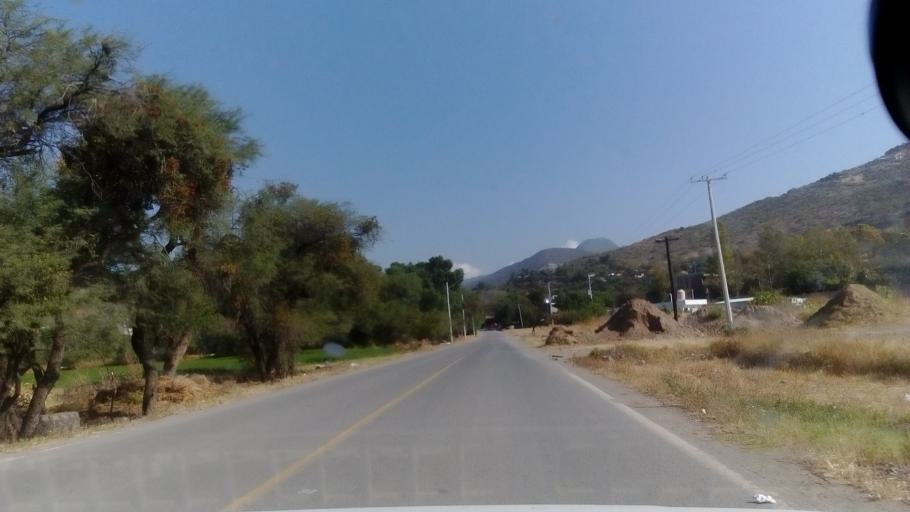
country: MX
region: Guanajuato
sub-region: Leon
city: Medina
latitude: 21.1440
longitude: -101.6098
